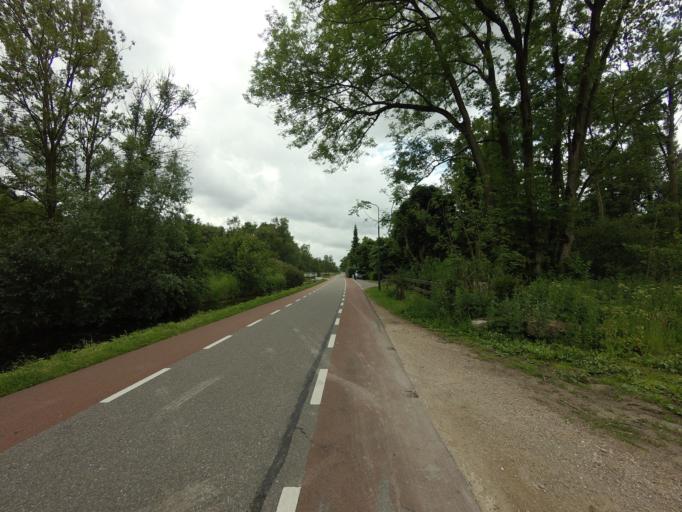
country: NL
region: North Holland
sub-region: Gemeente Wijdemeren
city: Oud-Loosdrecht
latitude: 52.2216
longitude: 5.0760
